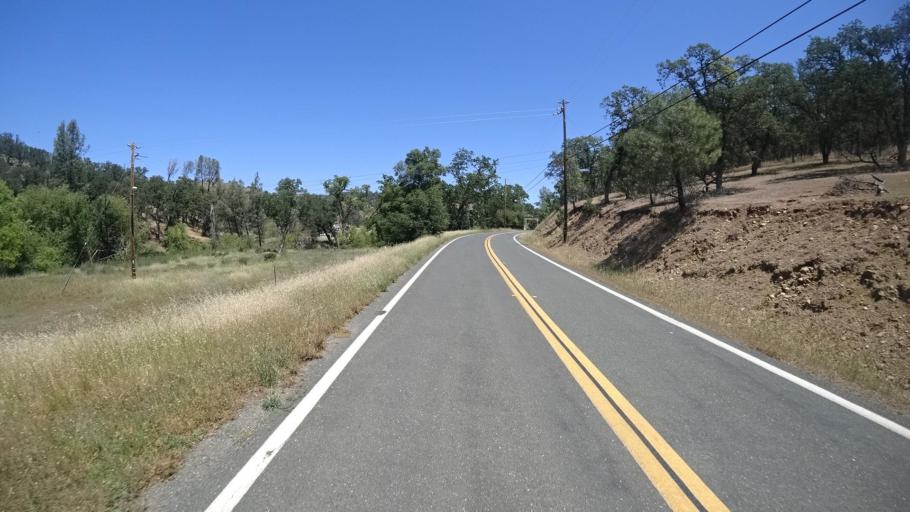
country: US
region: California
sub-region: Lake County
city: Hidden Valley Lake
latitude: 38.7989
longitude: -122.5477
